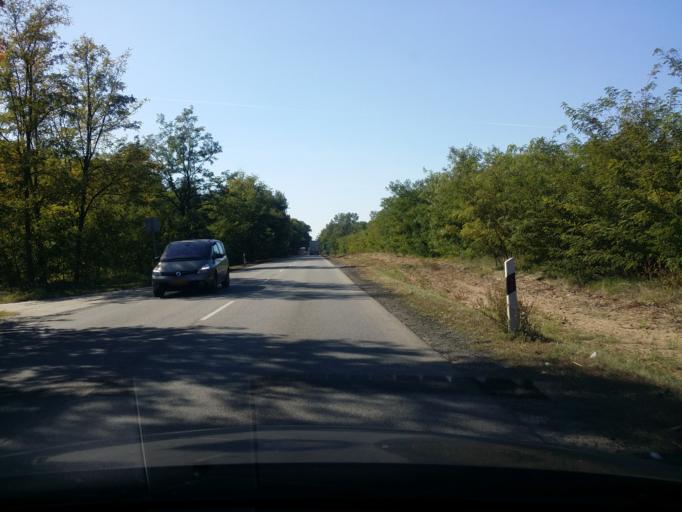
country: HU
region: Bacs-Kiskun
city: Lakitelek
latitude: 46.8714
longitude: 19.9677
